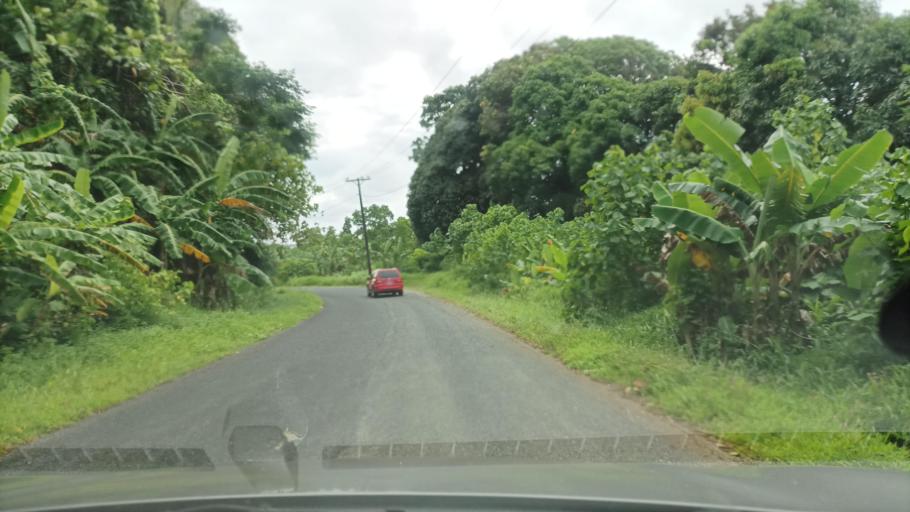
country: FM
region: Pohnpei
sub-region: Kolonia Municipality
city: Kolonia
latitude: 6.9696
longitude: 158.2582
